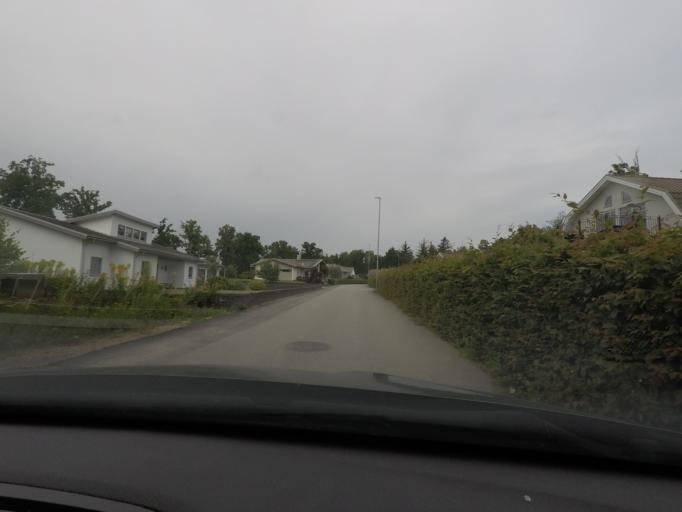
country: SE
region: Skane
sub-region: Osby Kommun
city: Osby
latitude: 56.3583
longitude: 13.9967
